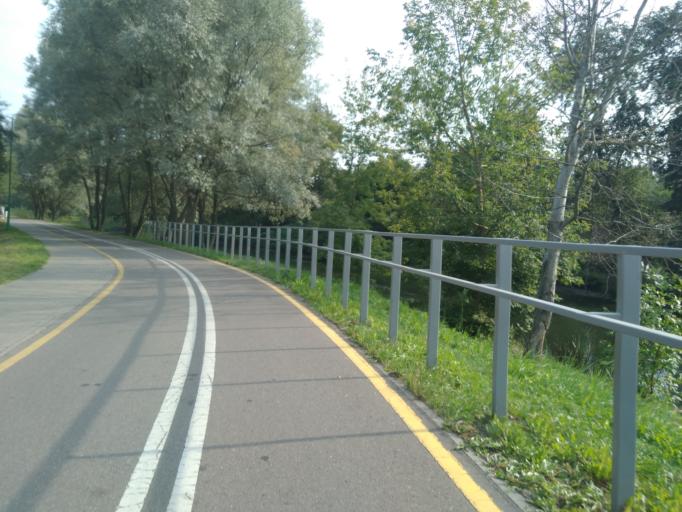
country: BY
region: Minsk
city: Minsk
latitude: 53.8720
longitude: 27.5836
